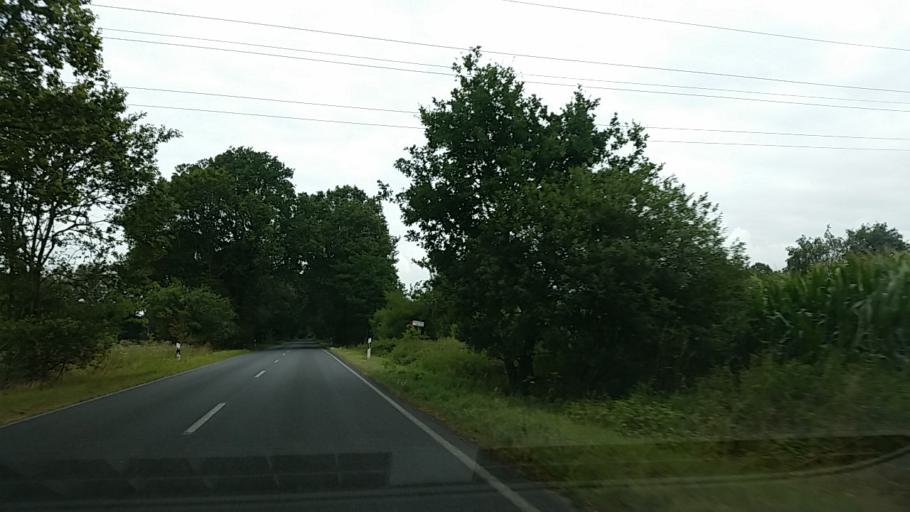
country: DE
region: Lower Saxony
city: Vollersode
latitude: 53.4077
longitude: 8.9179
